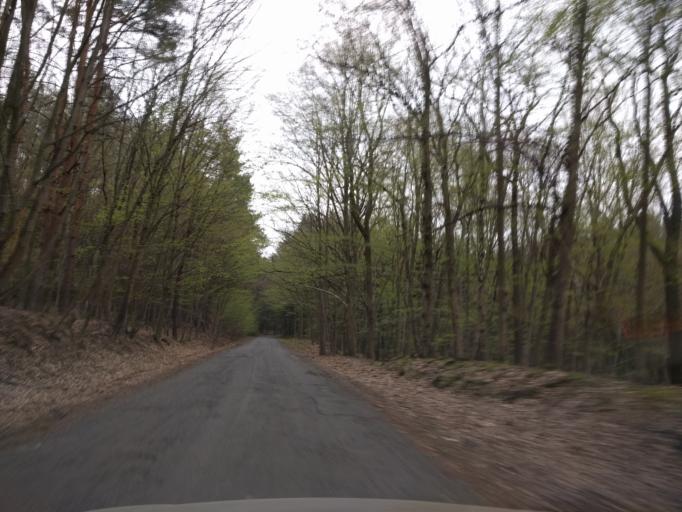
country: CZ
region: Central Bohemia
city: Kostelec nad Cernymi Lesy
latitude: 50.0160
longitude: 14.8202
